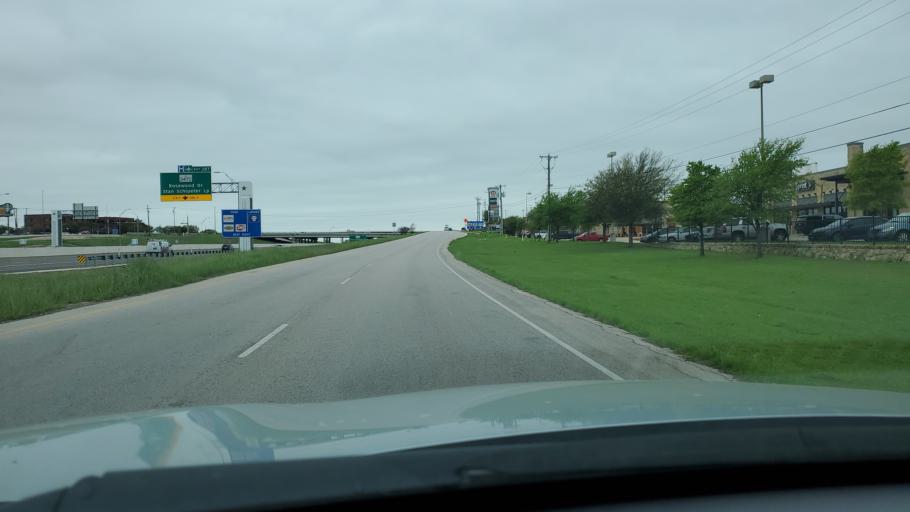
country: US
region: Texas
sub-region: Bell County
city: Harker Heights
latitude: 31.0716
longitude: -97.6650
